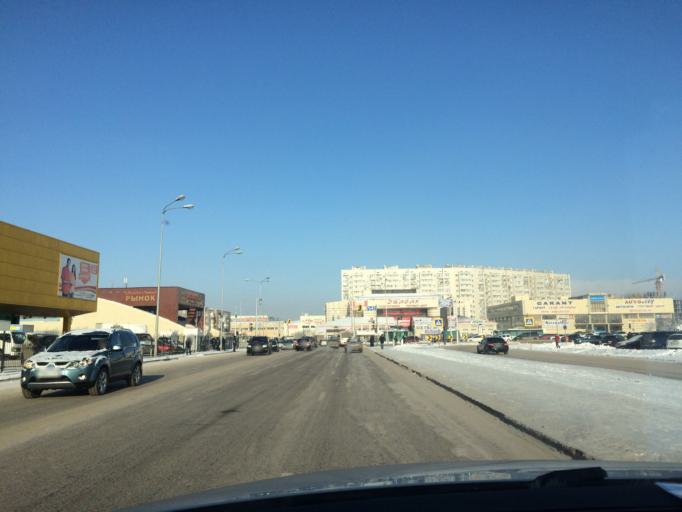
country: KZ
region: Astana Qalasy
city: Astana
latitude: 51.1776
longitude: 71.4370
